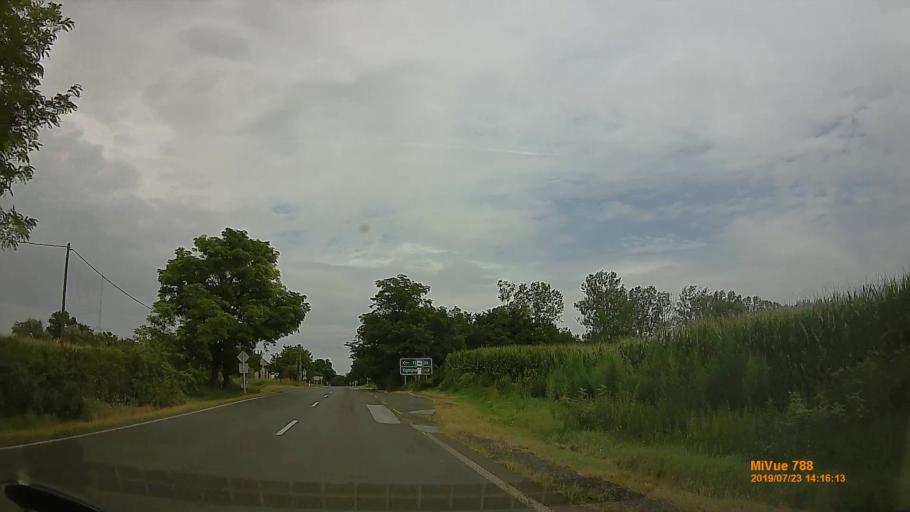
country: HU
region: Szabolcs-Szatmar-Bereg
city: Nagycserkesz
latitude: 47.9603
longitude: 21.5290
